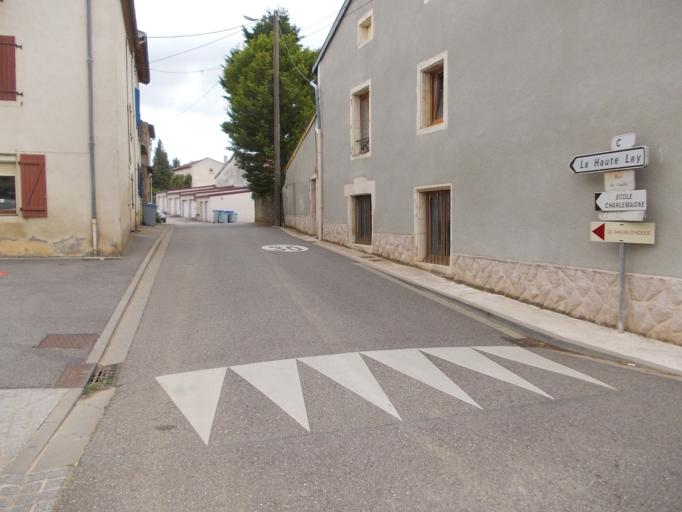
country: FR
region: Lorraine
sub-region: Departement de Meurthe-et-Moselle
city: Lay-Saint-Christophe
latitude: 48.7487
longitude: 6.1980
